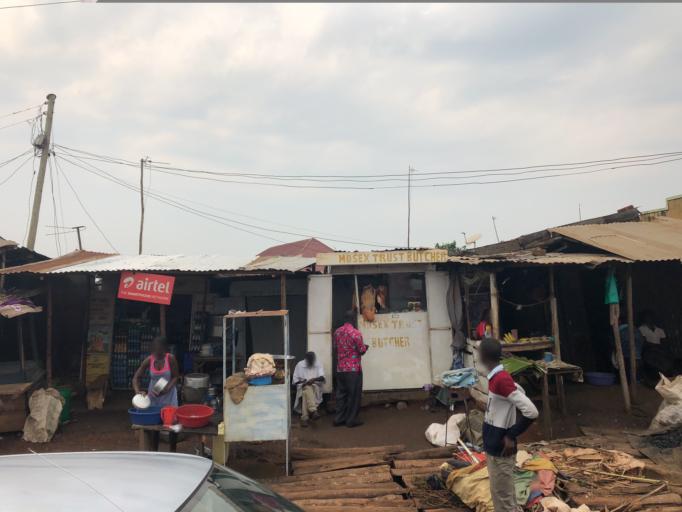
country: UG
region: Central Region
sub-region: Mukono District
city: Mukono
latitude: 0.3503
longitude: 32.7614
